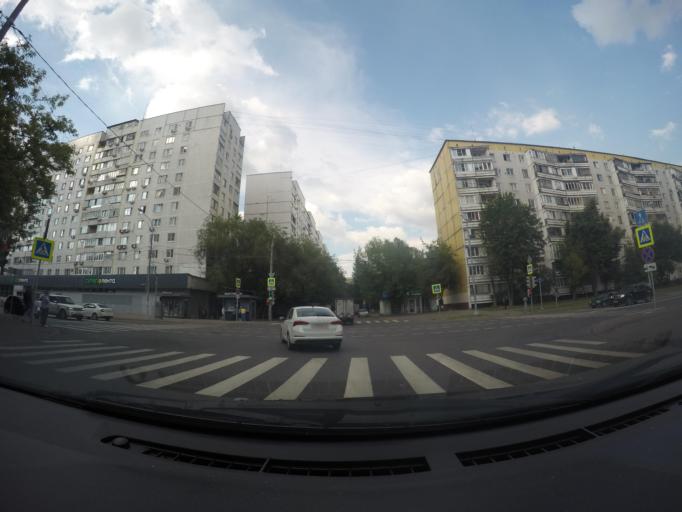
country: RU
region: Moscow
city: Kozeyevo
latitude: 55.8567
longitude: 37.6105
